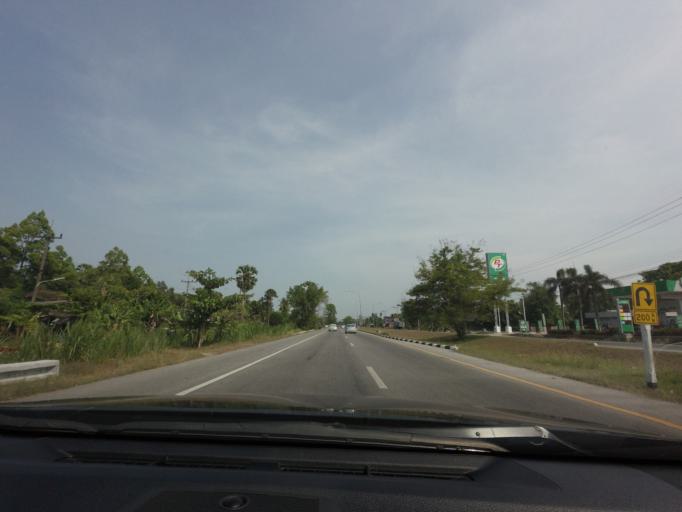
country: TH
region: Pattani
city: Yaring
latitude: 6.8312
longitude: 101.3892
